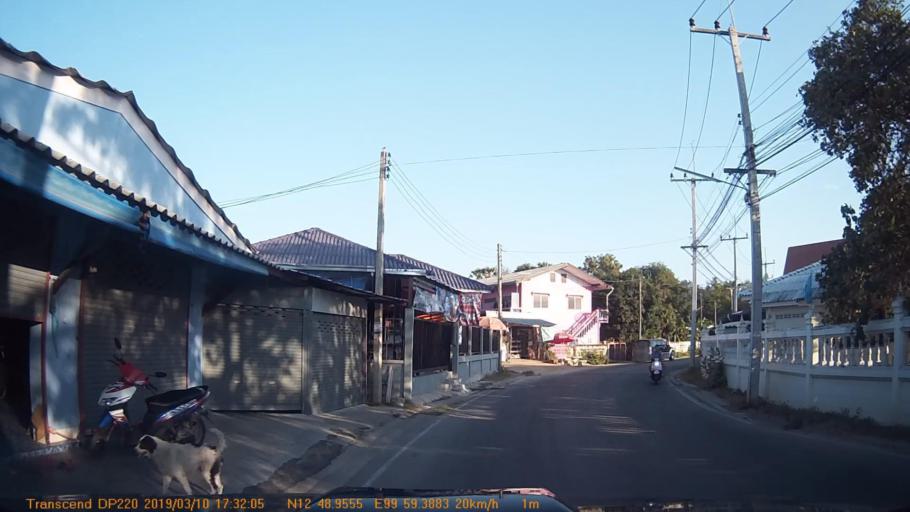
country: TH
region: Phetchaburi
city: Cha-am
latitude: 12.8158
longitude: 99.9899
